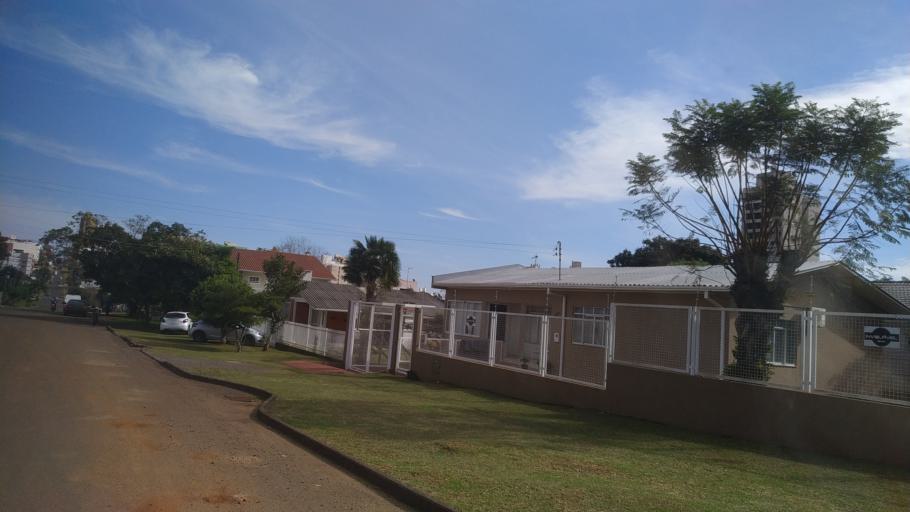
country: BR
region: Santa Catarina
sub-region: Chapeco
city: Chapeco
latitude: -27.1081
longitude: -52.6028
